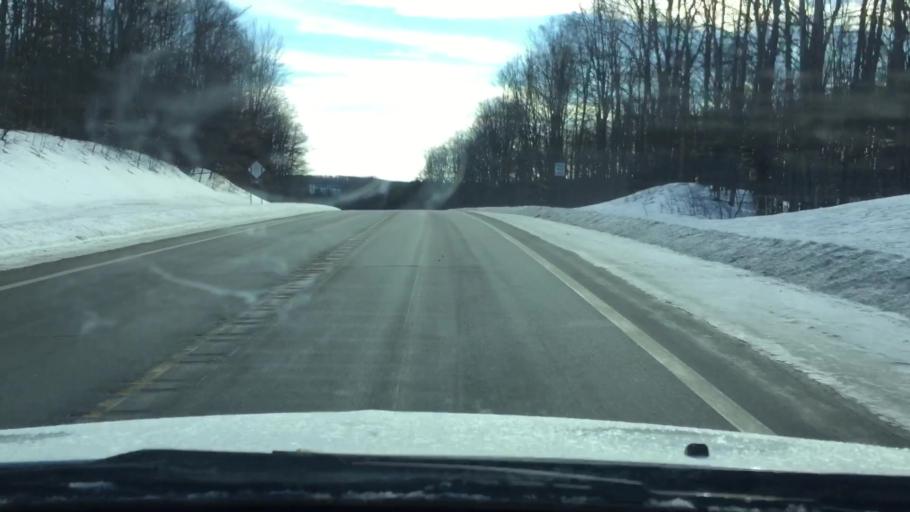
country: US
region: Michigan
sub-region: Antrim County
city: Mancelona
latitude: 44.9738
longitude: -85.0550
